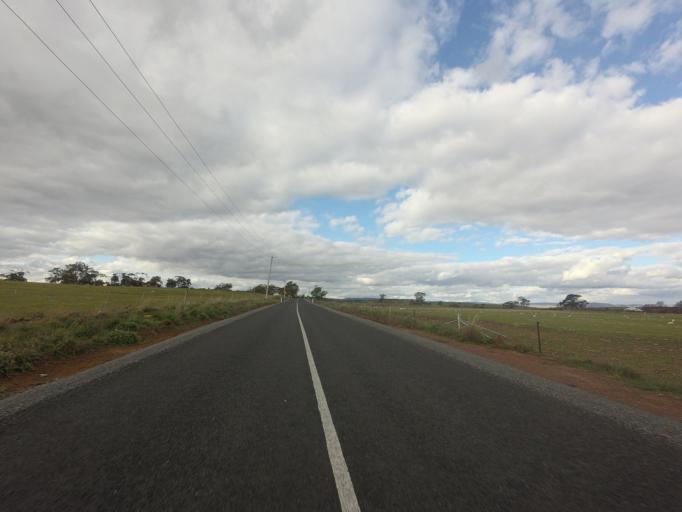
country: AU
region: Tasmania
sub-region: Northern Midlands
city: Evandale
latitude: -41.9094
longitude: 147.3838
